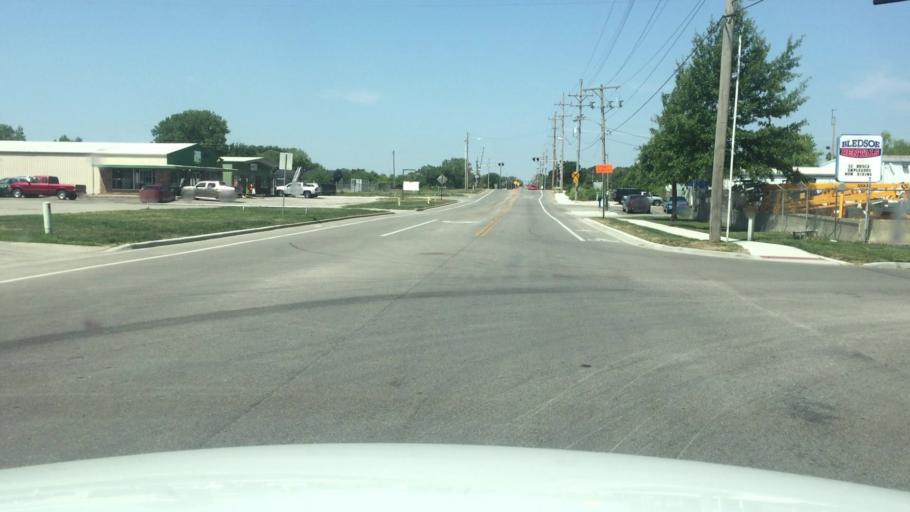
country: US
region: Kansas
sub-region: Johnson County
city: Olathe
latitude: 38.8692
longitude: -94.8204
